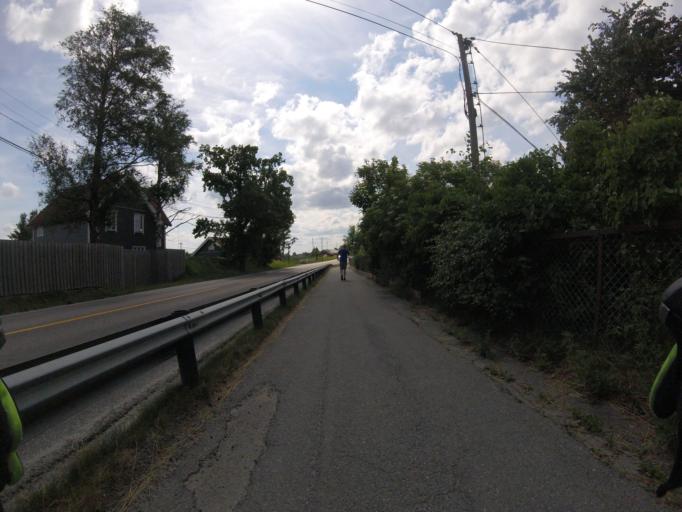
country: NO
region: Akershus
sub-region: Skedsmo
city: Lillestrom
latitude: 59.9771
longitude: 11.0565
